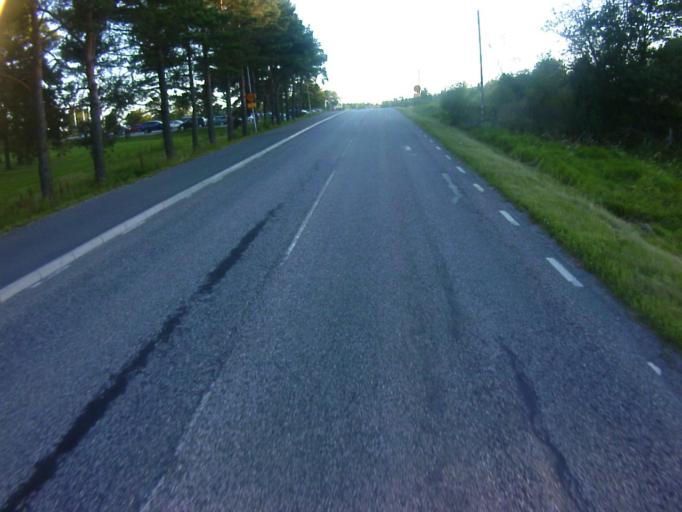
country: SE
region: Soedermanland
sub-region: Eskilstuna Kommun
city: Torshalla
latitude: 59.4137
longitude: 16.4418
